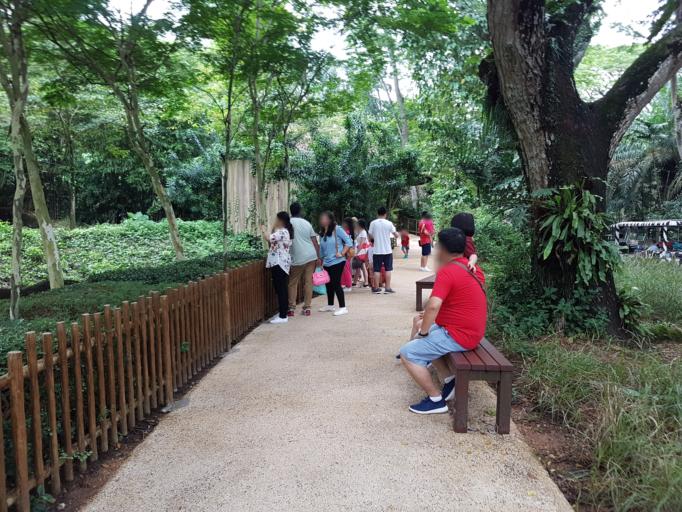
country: MY
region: Johor
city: Johor Bahru
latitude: 1.4028
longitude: 103.7937
